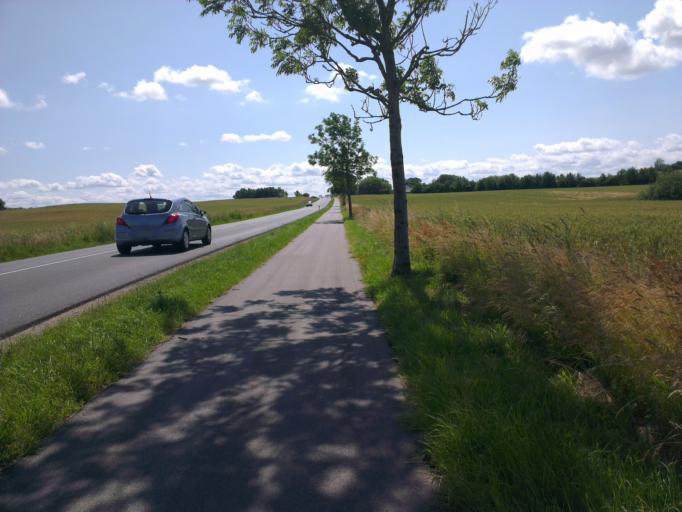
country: DK
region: Capital Region
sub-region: Frederikssund Kommune
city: Skibby
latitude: 55.7730
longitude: 11.9066
